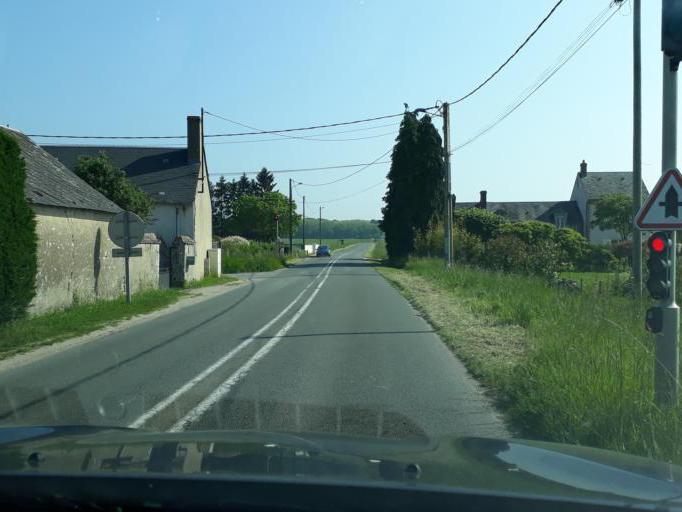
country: FR
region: Centre
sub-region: Departement du Loiret
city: Vennecy
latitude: 47.9484
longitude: 2.0680
